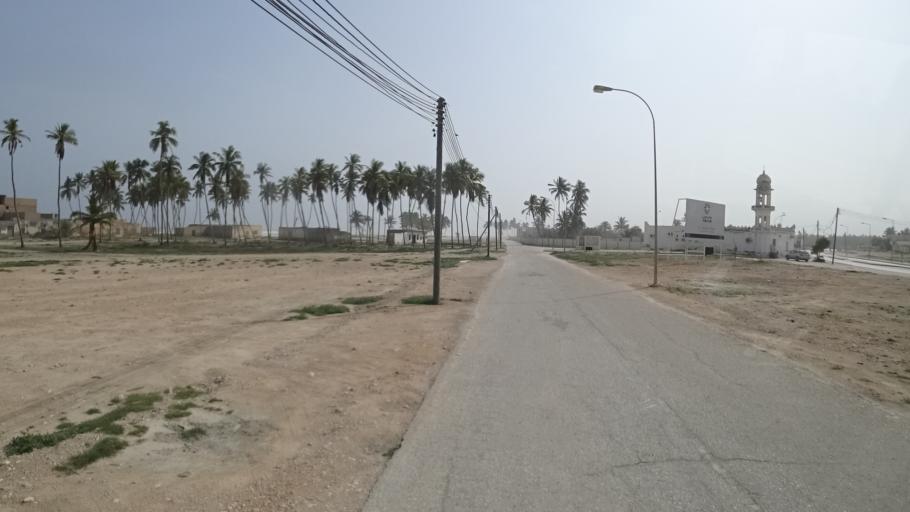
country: OM
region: Zufar
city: Salalah
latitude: 17.0027
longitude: 54.1124
